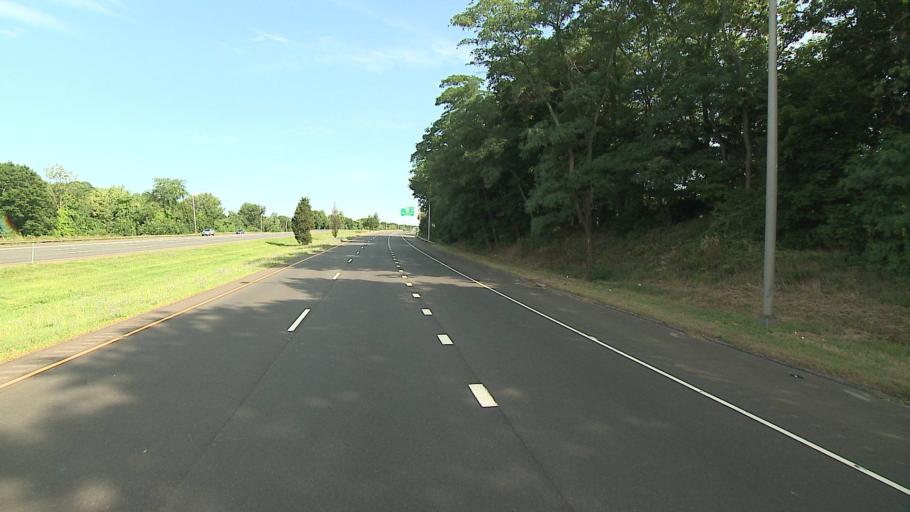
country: US
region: Connecticut
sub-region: Fairfield County
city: Norwalk
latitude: 41.1234
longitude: -73.4240
